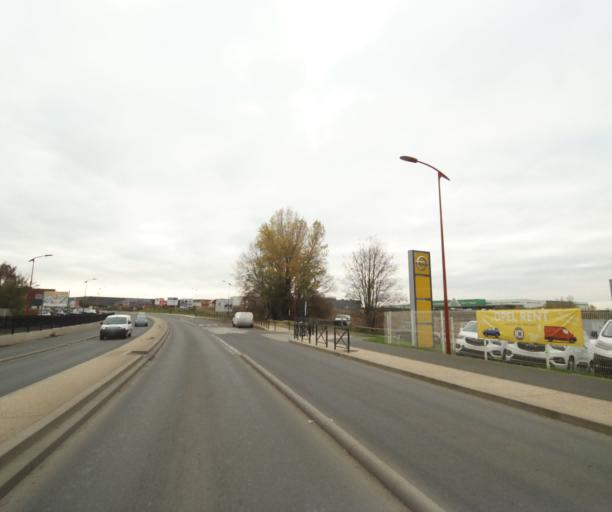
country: FR
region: Ile-de-France
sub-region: Departement du Val-d'Oise
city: Gonesse
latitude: 48.9835
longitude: 2.4410
